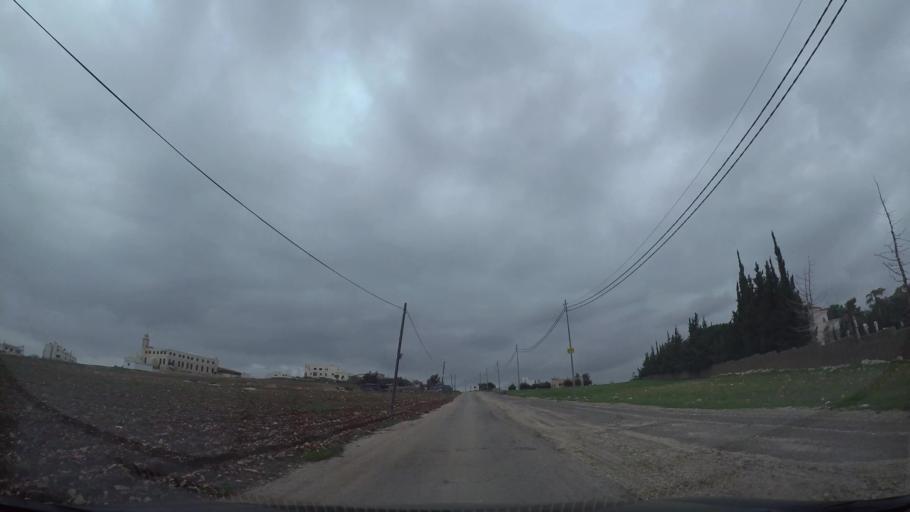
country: JO
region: Amman
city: Umm as Summaq
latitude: 31.9282
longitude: 35.8581
